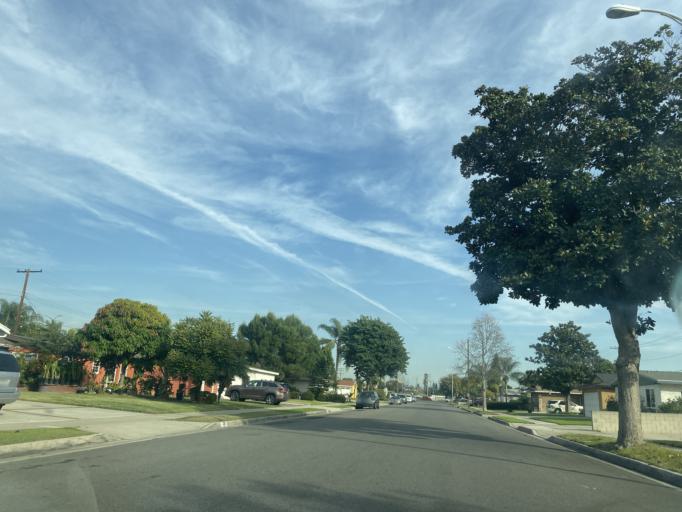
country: US
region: California
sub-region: Orange County
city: Buena Park
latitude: 33.8489
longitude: -117.9619
